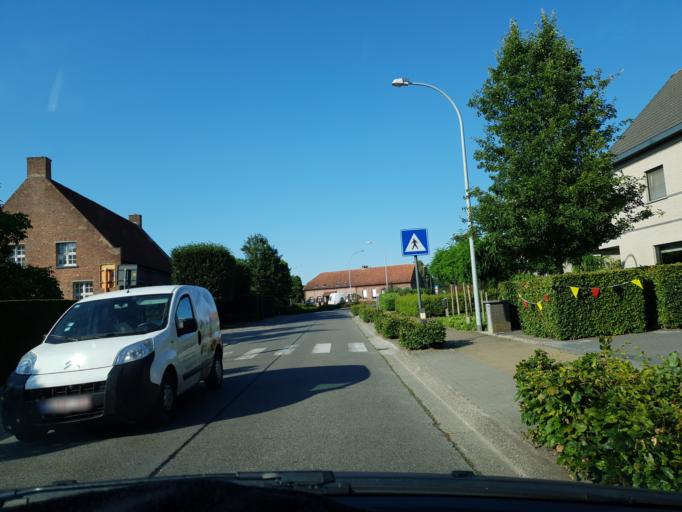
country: BE
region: Flanders
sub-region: Provincie Antwerpen
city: Hoogstraten
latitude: 51.3982
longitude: 4.8019
